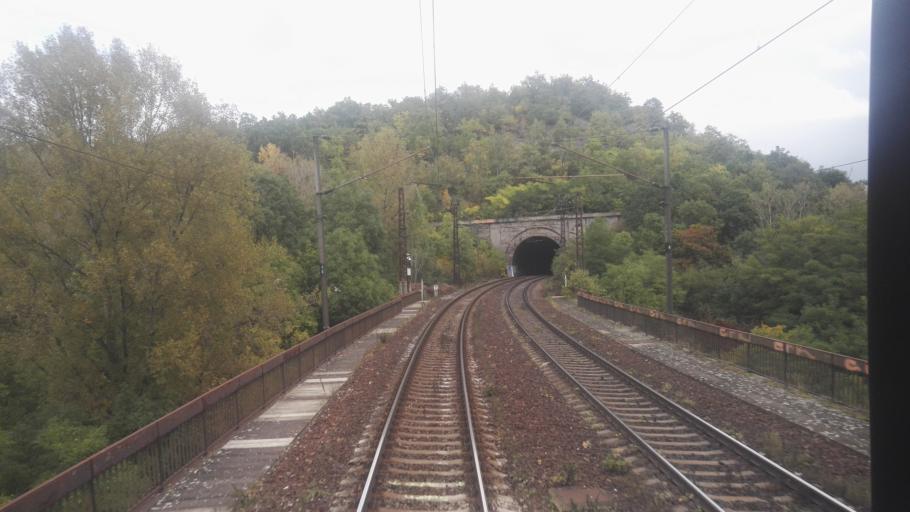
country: CZ
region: Praha
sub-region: Praha 8
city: Karlin
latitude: 50.1138
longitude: 14.4524
